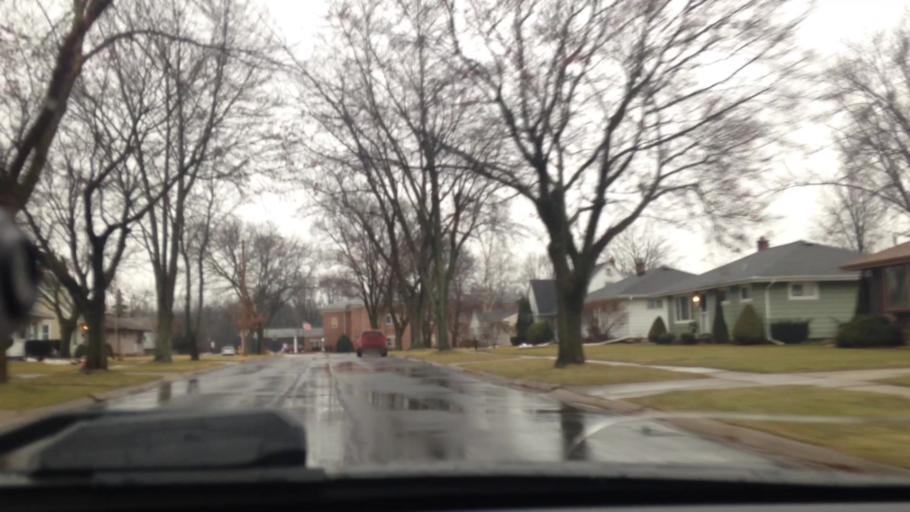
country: US
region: Wisconsin
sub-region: Waukesha County
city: Menomonee Falls
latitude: 43.1716
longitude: -88.1191
